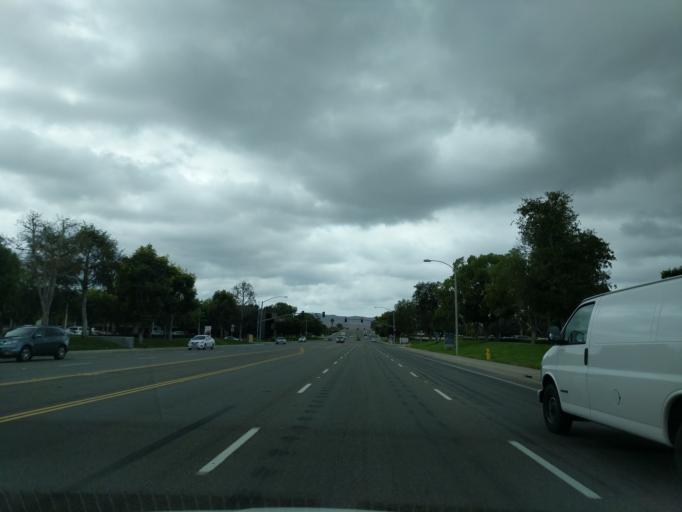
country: US
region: California
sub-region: Orange County
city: Lake Forest
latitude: 33.6527
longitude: -117.7166
